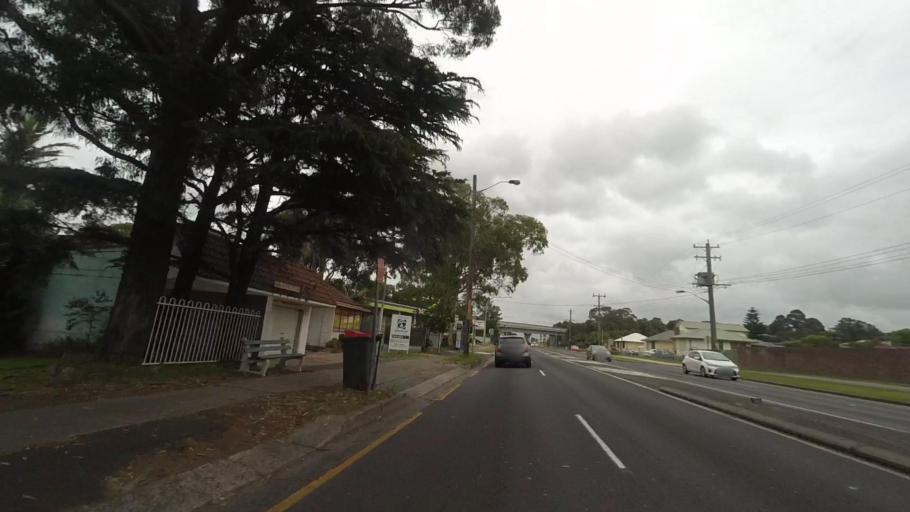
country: AU
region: New South Wales
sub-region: Wollongong
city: Cordeaux Heights
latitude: -34.4594
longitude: 150.8407
